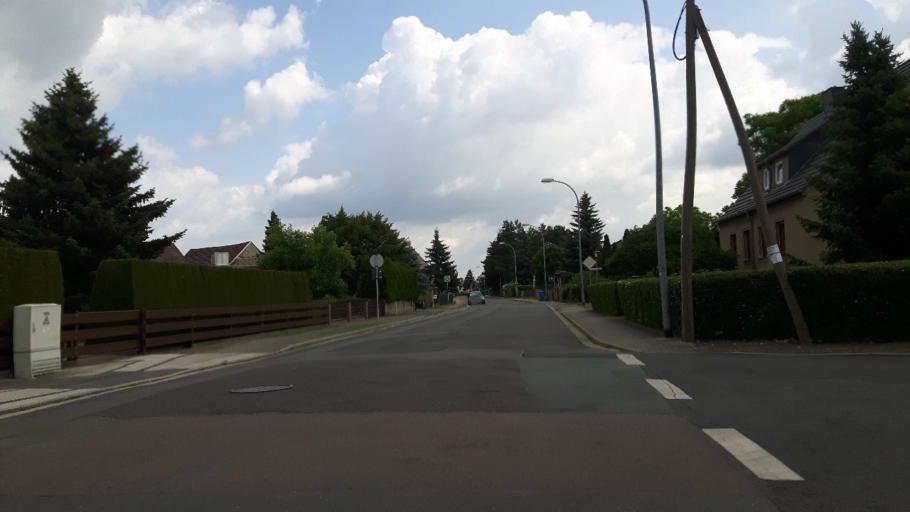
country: DE
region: Saxony
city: Delitzsch
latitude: 51.5340
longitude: 12.3513
